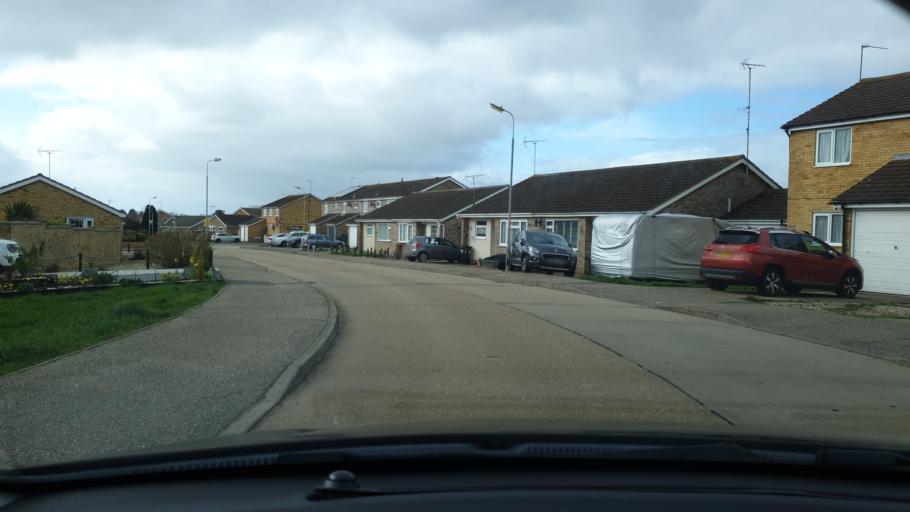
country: GB
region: England
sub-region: Essex
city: Little Clacton
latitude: 51.8156
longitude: 1.1558
